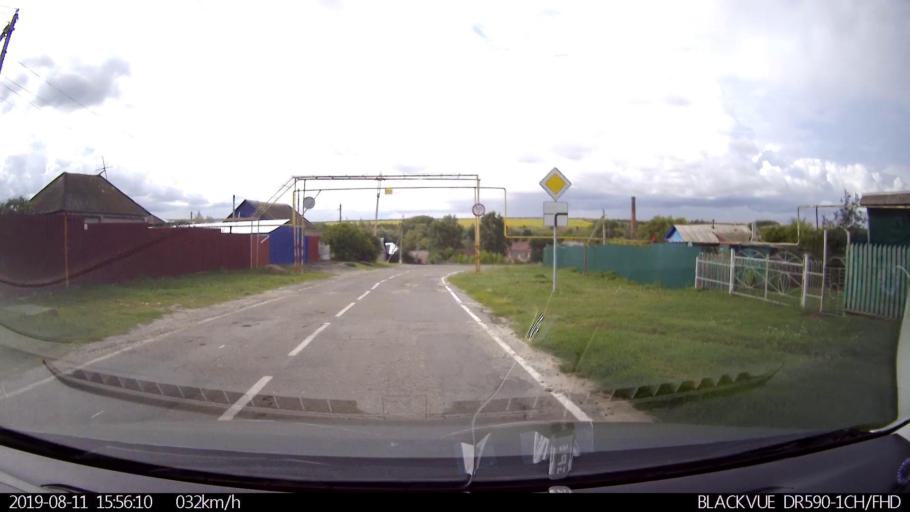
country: RU
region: Ulyanovsk
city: Ignatovka
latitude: 53.9477
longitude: 47.6492
